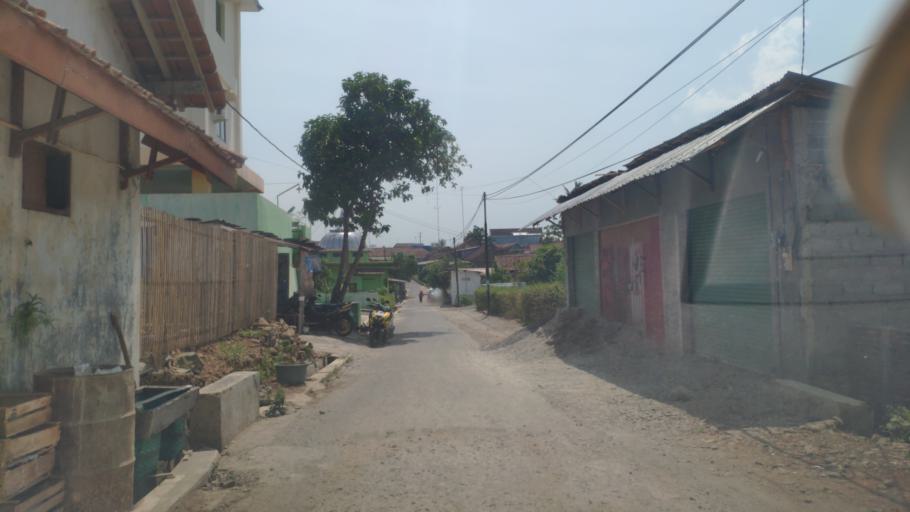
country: ID
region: Central Java
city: Wonosobo
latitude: -7.3983
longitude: 109.6990
